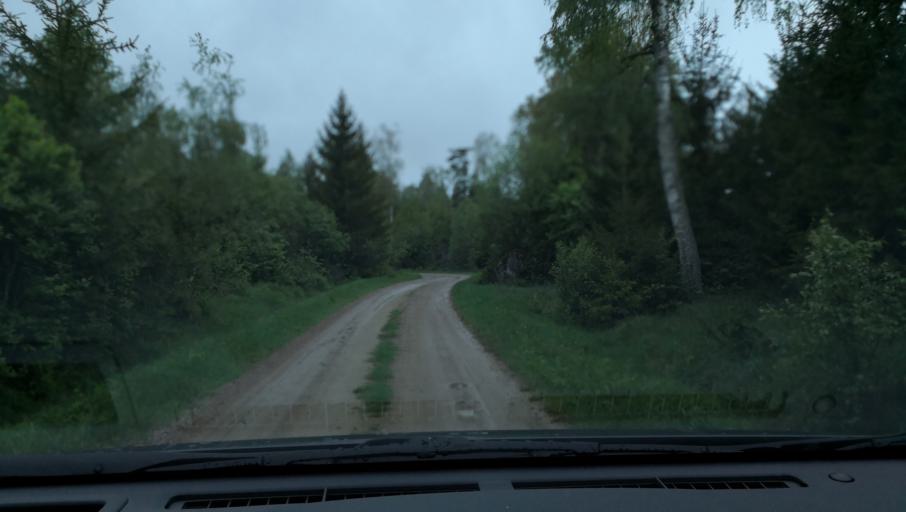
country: SE
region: Uppsala
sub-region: Enkopings Kommun
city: Orsundsbro
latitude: 59.9239
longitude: 17.3403
